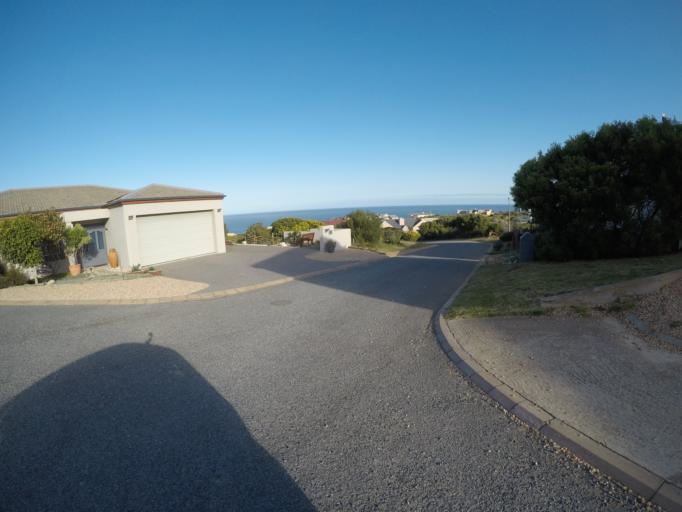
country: ZA
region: Western Cape
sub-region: Eden District Municipality
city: Riversdale
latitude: -34.4183
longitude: 21.3462
